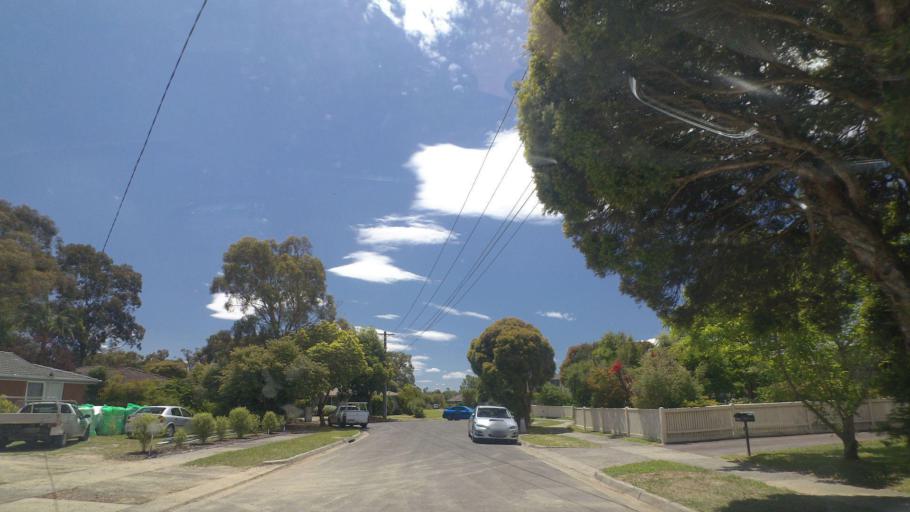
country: AU
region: Victoria
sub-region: Maroondah
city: Kilsyth South
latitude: -37.8123
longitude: 145.3135
